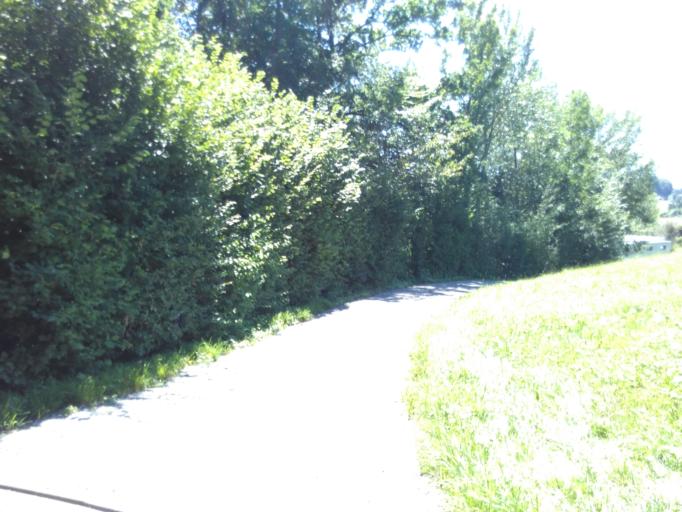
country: CH
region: Zurich
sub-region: Bezirk Hinwil
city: Rueti / Dorfzentrum, Suedl. Teil
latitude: 47.2528
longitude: 8.8519
